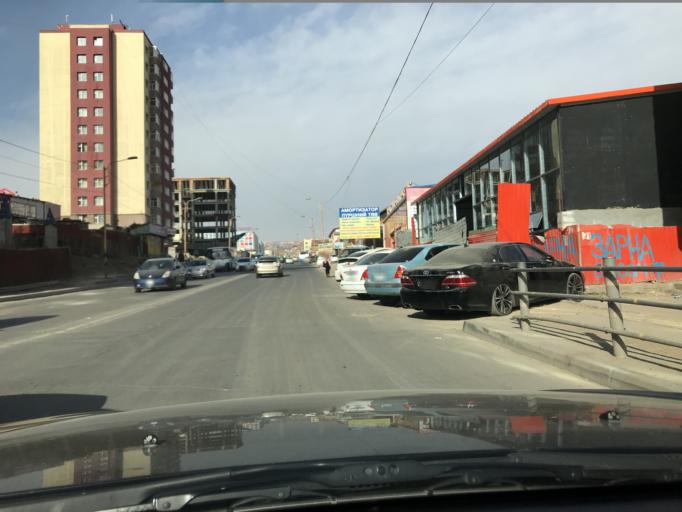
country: MN
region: Ulaanbaatar
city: Ulaanbaatar
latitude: 47.9260
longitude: 106.8948
